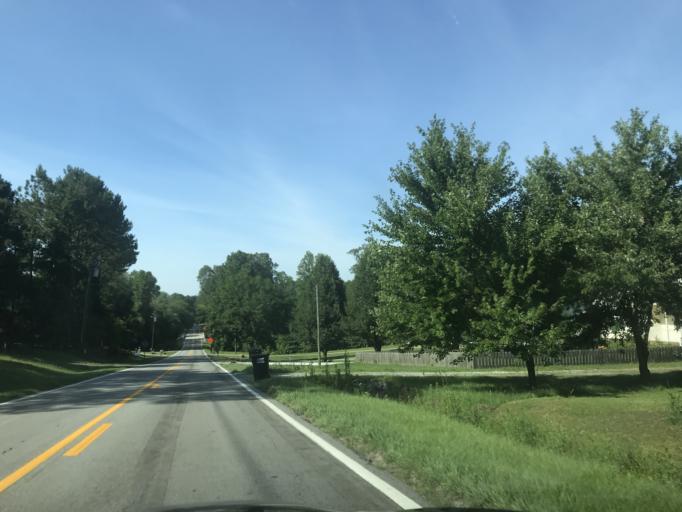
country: US
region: North Carolina
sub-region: Johnston County
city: Clayton
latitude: 35.5972
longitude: -78.5364
